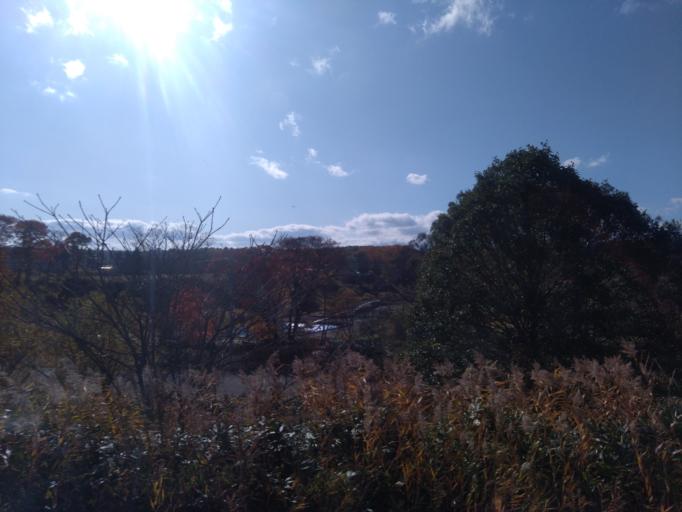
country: JP
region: Hokkaido
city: Kitahiroshima
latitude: 42.9908
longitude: 141.5560
